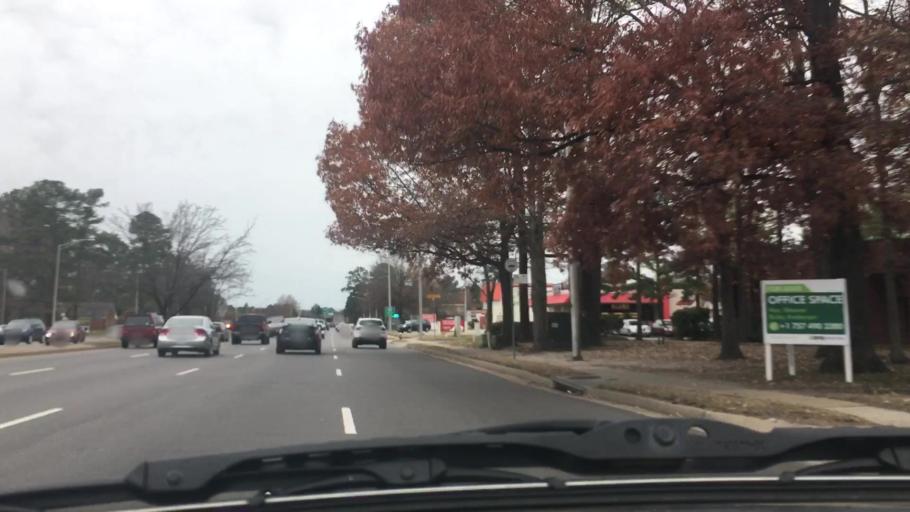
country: US
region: Virginia
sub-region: City of Chesapeake
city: Chesapeake
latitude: 36.8270
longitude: -76.1318
